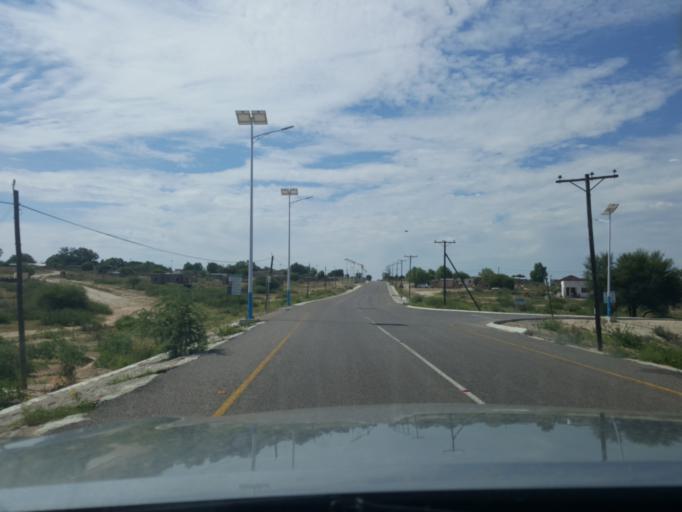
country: BW
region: Kweneng
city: Letlhakeng
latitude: -24.0906
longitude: 25.0302
